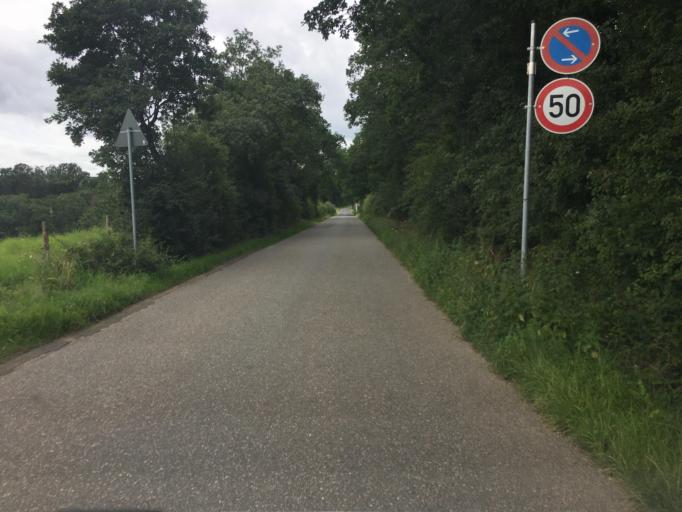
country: DE
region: North Rhine-Westphalia
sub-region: Regierungsbezirk Koln
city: Bad Munstereifel
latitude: 50.5943
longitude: 6.8345
